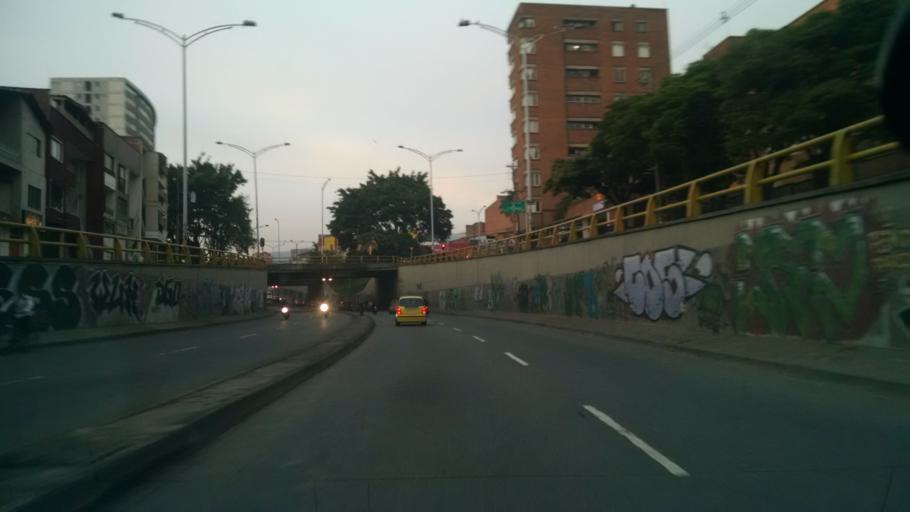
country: CO
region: Antioquia
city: Medellin
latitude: 6.2518
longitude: -75.6019
